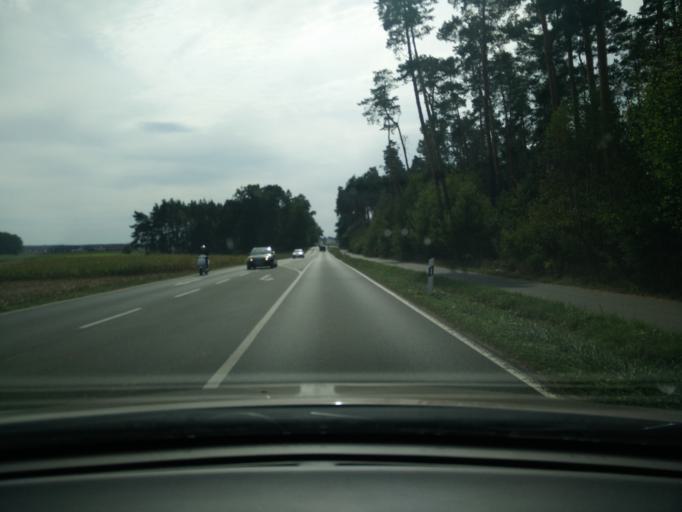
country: DE
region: Bavaria
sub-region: Regierungsbezirk Mittelfranken
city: Veitsbronn
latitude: 49.5011
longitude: 10.8797
